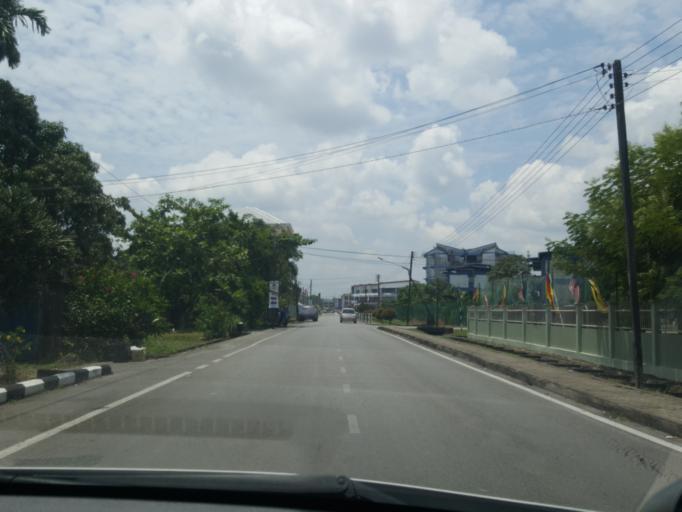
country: MY
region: Sarawak
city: Sarikei
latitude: 2.1286
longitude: 111.5197
